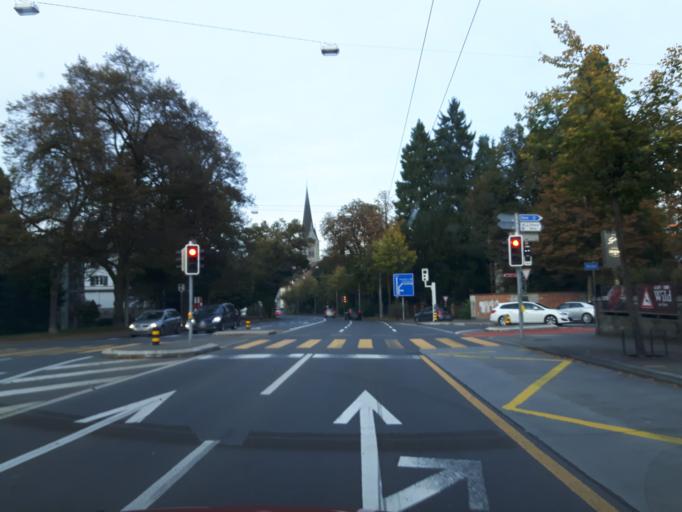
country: CH
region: Lucerne
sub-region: Lucerne-Stadt District
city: Luzern
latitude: 47.0402
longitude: 8.3013
